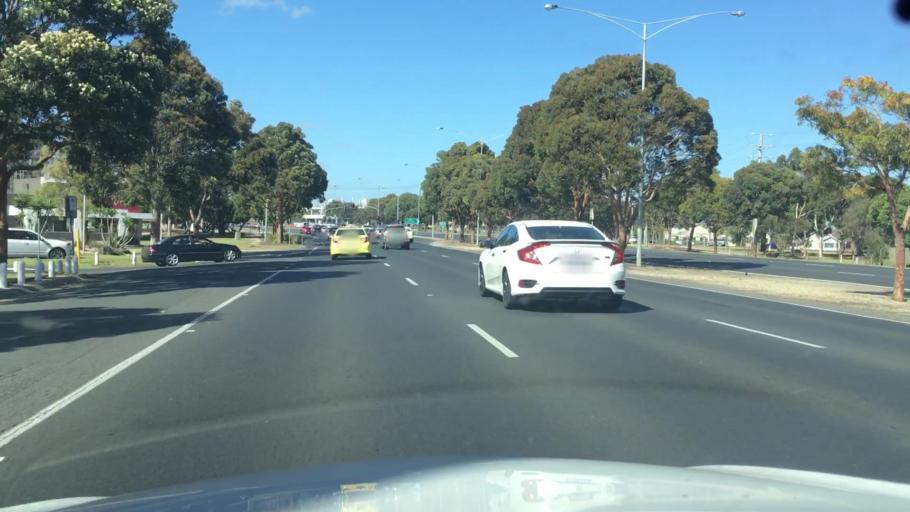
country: AU
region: Victoria
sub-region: Greater Geelong
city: Bell Park
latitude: -38.0827
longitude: 144.3604
